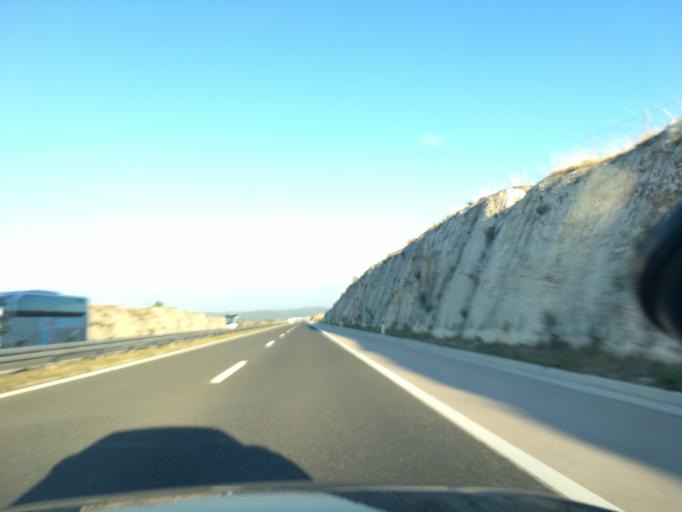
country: HR
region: Sibensko-Kniniska
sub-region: Grad Sibenik
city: Brodarica
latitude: 43.7039
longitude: 16.0075
